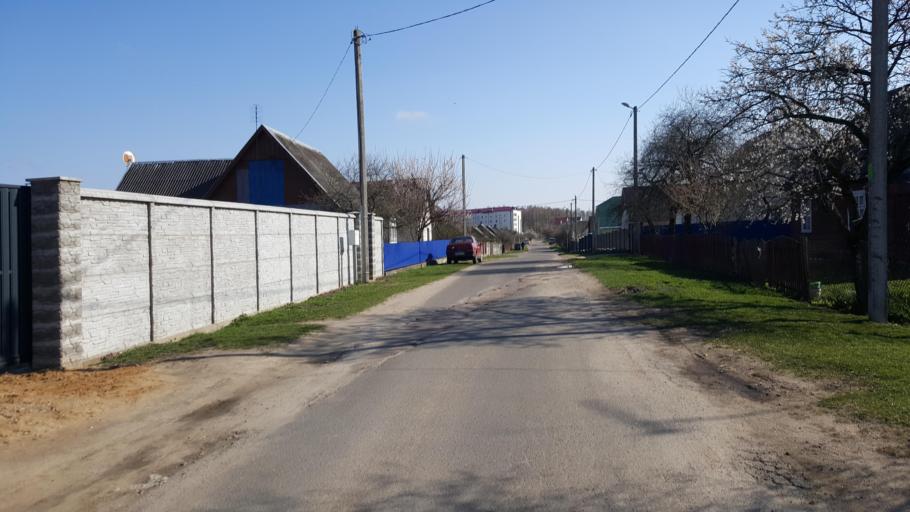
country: BY
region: Brest
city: Kamyanyets
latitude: 52.3973
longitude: 23.8194
